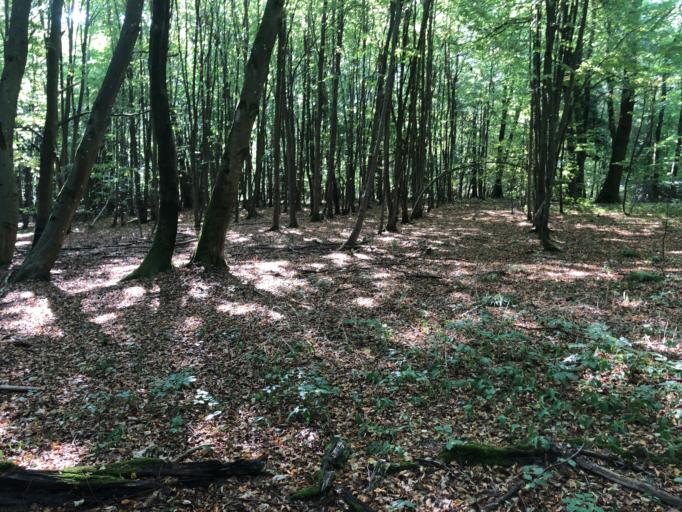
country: DE
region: Baden-Wuerttemberg
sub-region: Tuebingen Region
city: Tuebingen
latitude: 48.5086
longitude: 9.0838
